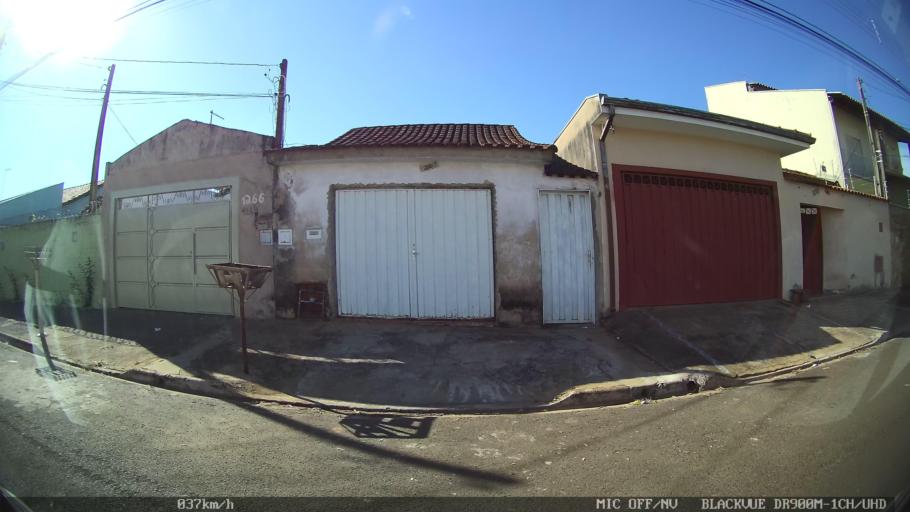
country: BR
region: Sao Paulo
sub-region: Franca
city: Franca
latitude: -20.4882
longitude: -47.4144
